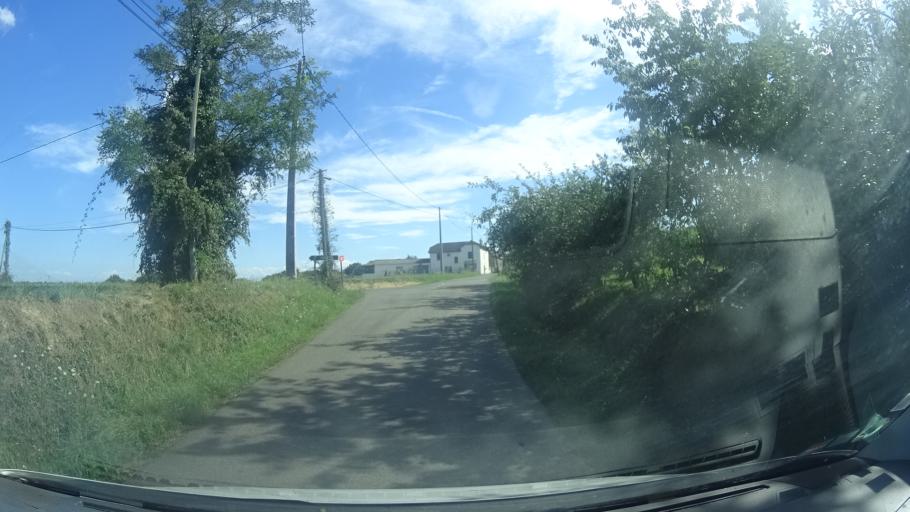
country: FR
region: Aquitaine
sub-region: Departement des Pyrenees-Atlantiques
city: Mont
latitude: 43.4904
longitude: -0.6635
